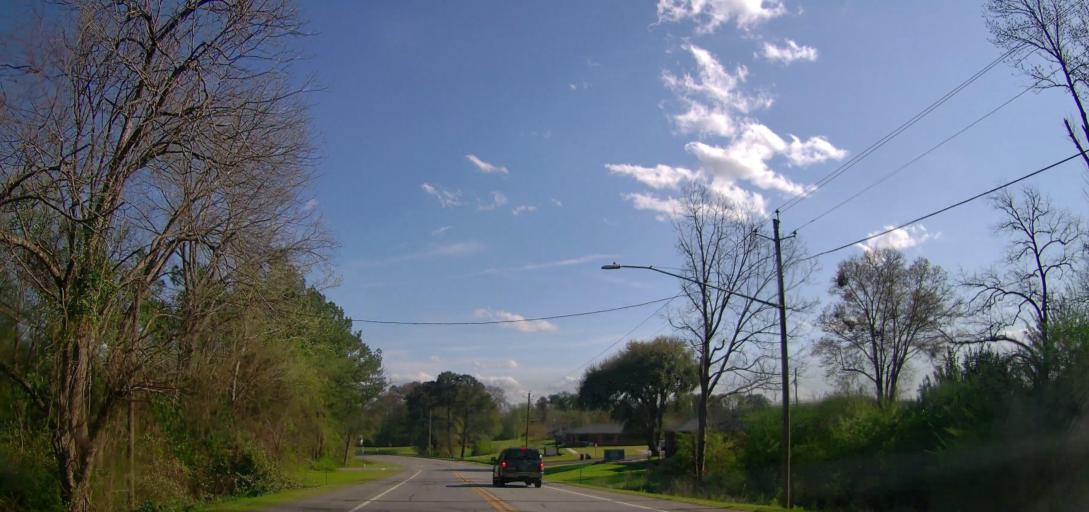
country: US
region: Georgia
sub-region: Baldwin County
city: Milledgeville
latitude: 33.0831
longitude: -83.2451
